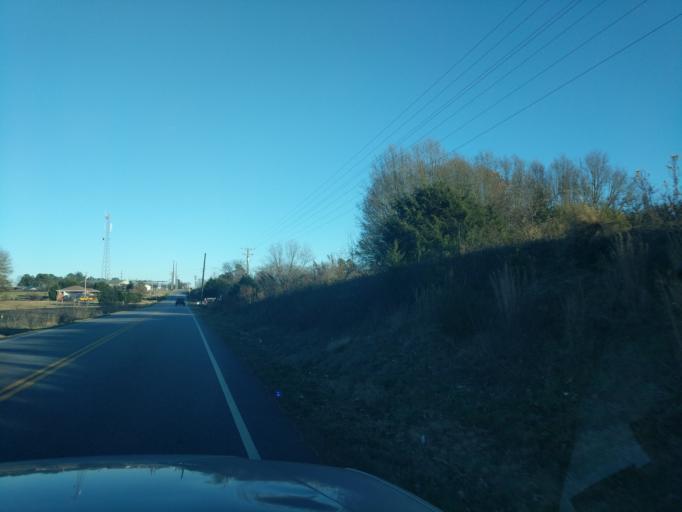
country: US
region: South Carolina
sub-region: Oconee County
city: Westminster
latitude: 34.6009
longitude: -83.0213
